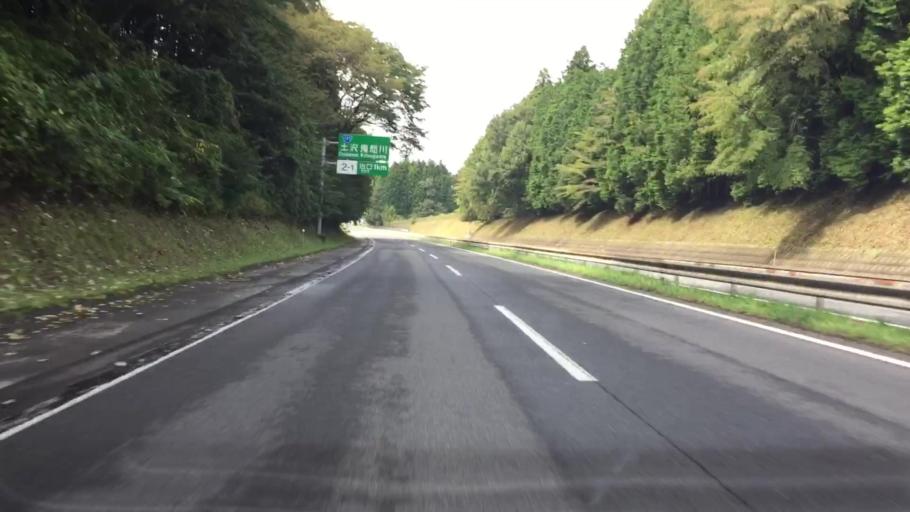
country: JP
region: Tochigi
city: Imaichi
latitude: 36.7011
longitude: 139.7268
